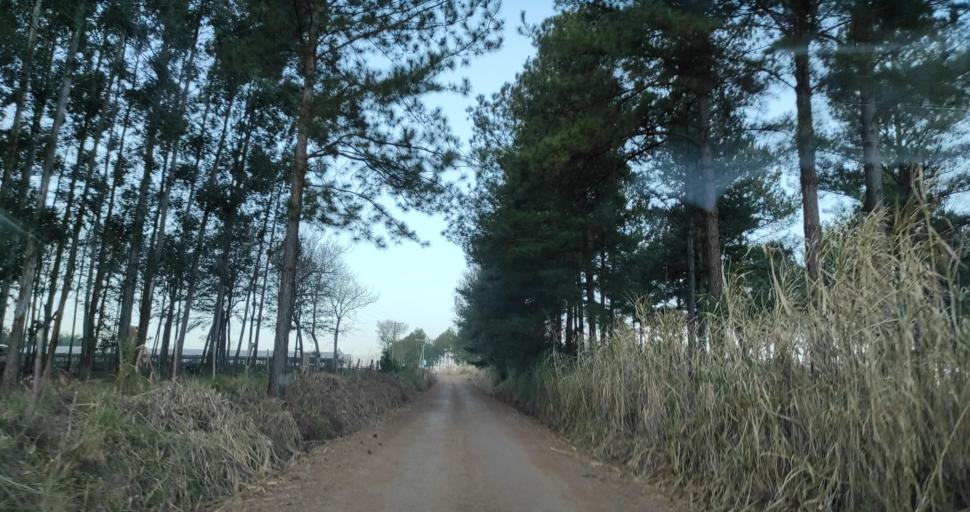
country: AR
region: Misiones
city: Capiovi
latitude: -26.8935
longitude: -55.0511
